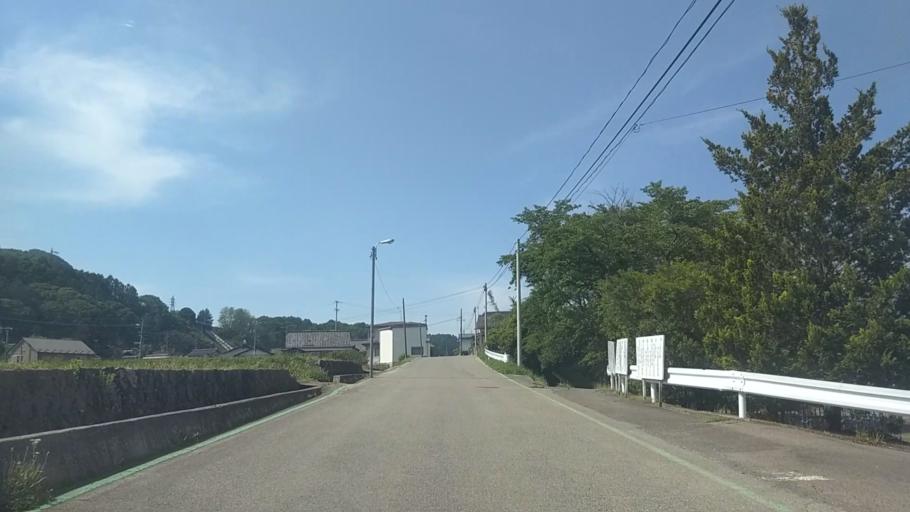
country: JP
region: Nagano
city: Saku
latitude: 36.1347
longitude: 138.4753
